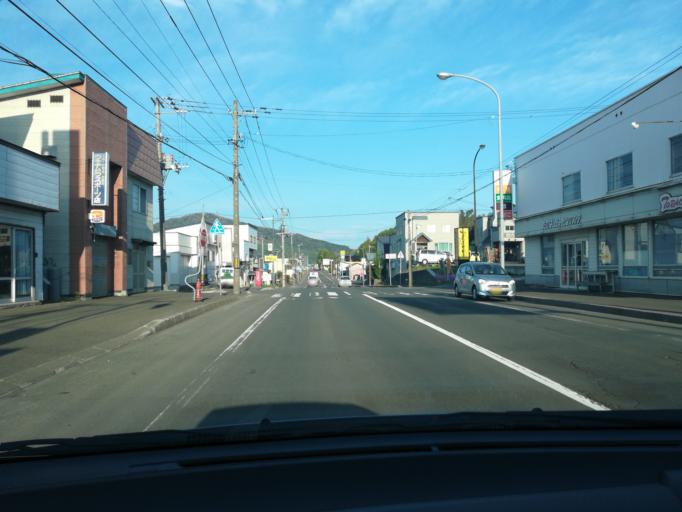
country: JP
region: Hokkaido
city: Shimo-furano
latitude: 43.1632
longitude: 142.5691
